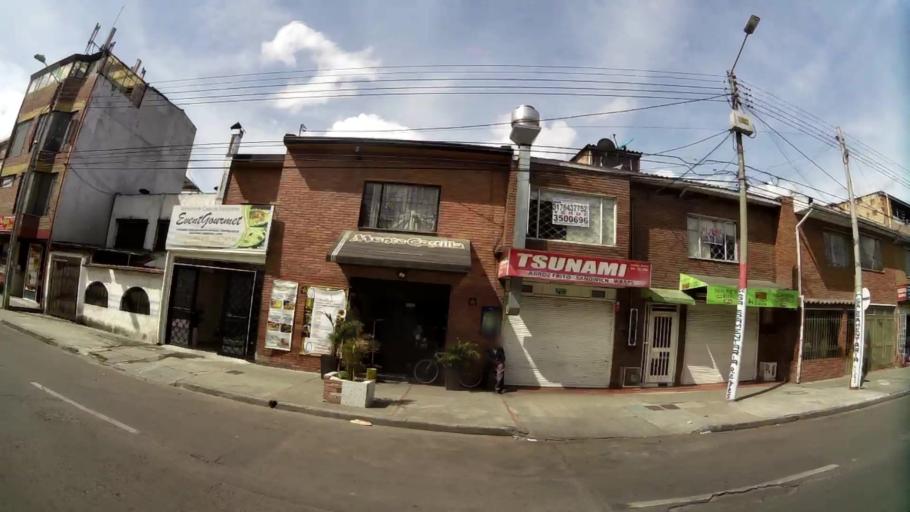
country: CO
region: Bogota D.C.
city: Bogota
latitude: 4.6431
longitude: -74.1422
